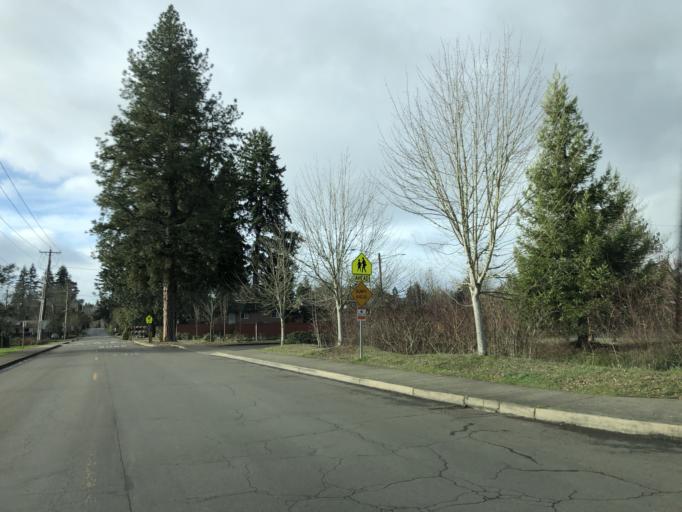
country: US
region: Oregon
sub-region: Washington County
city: Tigard
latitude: 45.4299
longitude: -122.7781
